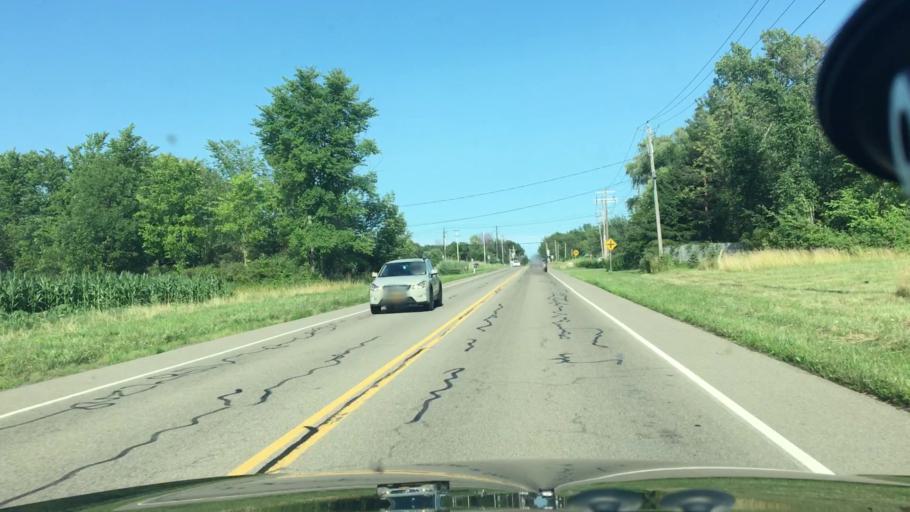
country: US
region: New York
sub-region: Erie County
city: Angola
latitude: 42.6525
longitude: -79.0149
